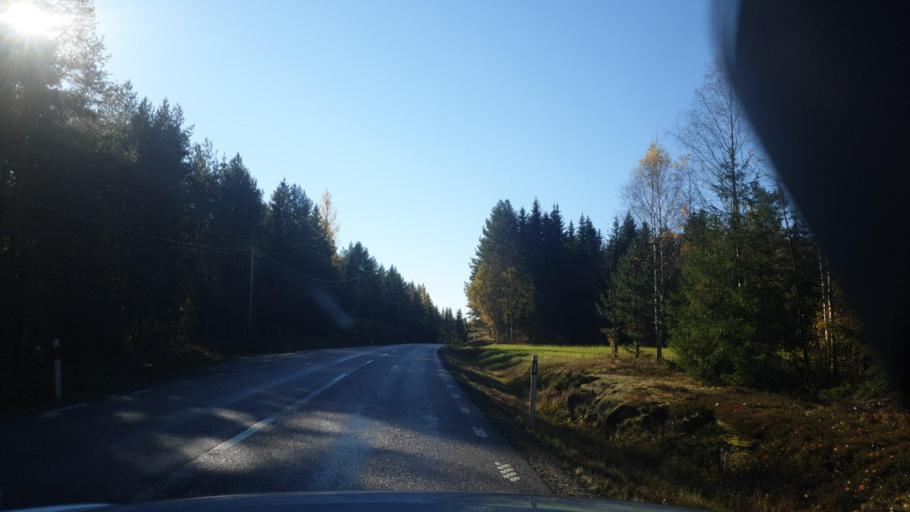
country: SE
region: Vaermland
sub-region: Arvika Kommun
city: Arvika
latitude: 59.5145
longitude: 12.7770
